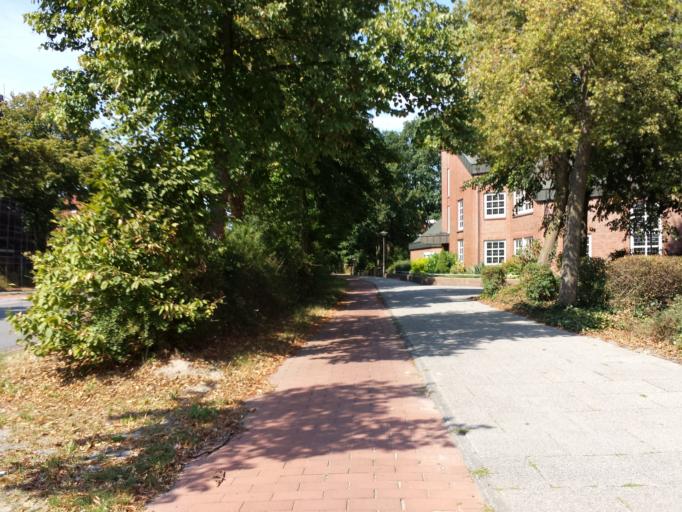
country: DE
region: Bremen
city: Bremen
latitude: 53.0362
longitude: 8.8402
